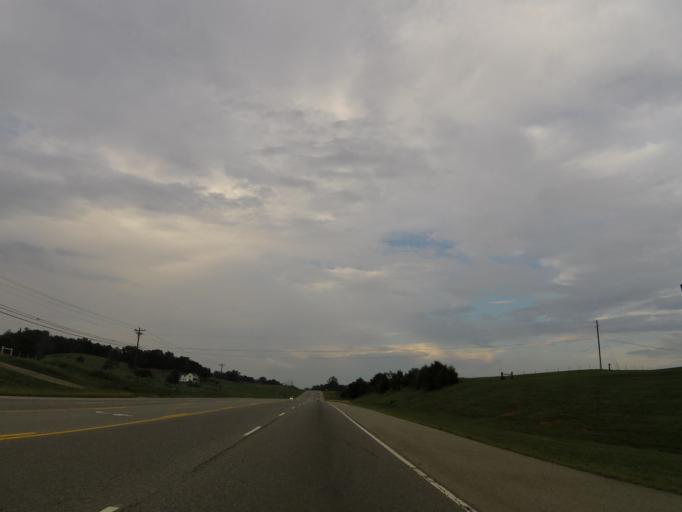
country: US
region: Tennessee
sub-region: Loudon County
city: Greenback
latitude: 35.6828
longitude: -84.0668
